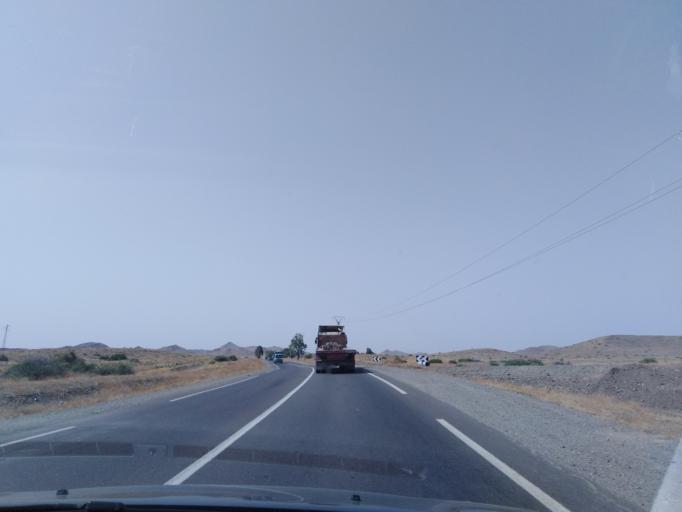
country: MA
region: Marrakech-Tensift-Al Haouz
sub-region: Kelaa-Des-Sraghna
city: Sidi Bou Othmane
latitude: 31.8128
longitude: -7.9762
